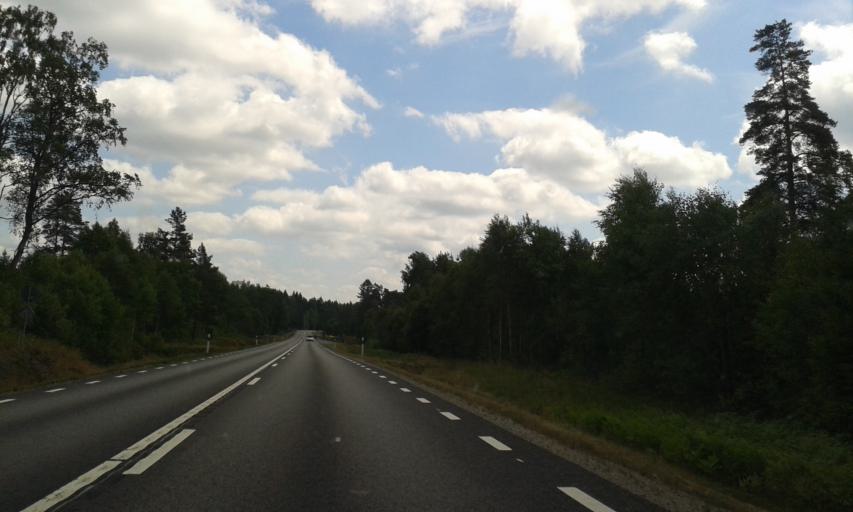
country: SE
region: Joenkoeping
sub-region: Varnamo Kommun
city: Rydaholm
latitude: 56.9280
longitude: 14.4049
